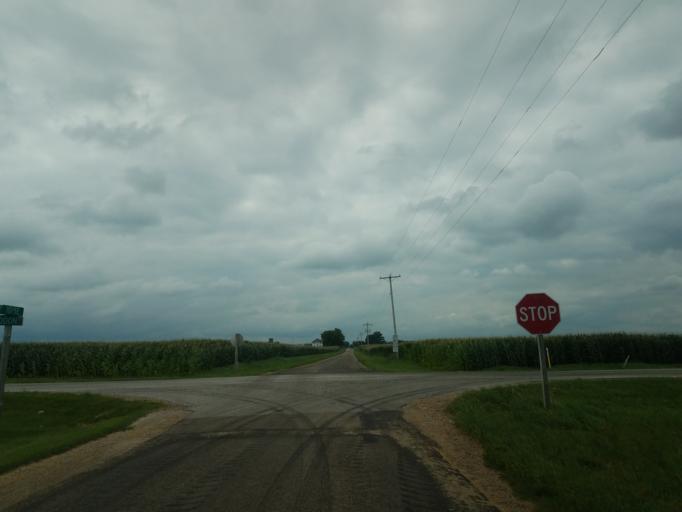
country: US
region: Illinois
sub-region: McLean County
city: Twin Grove
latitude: 40.4297
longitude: -89.0623
